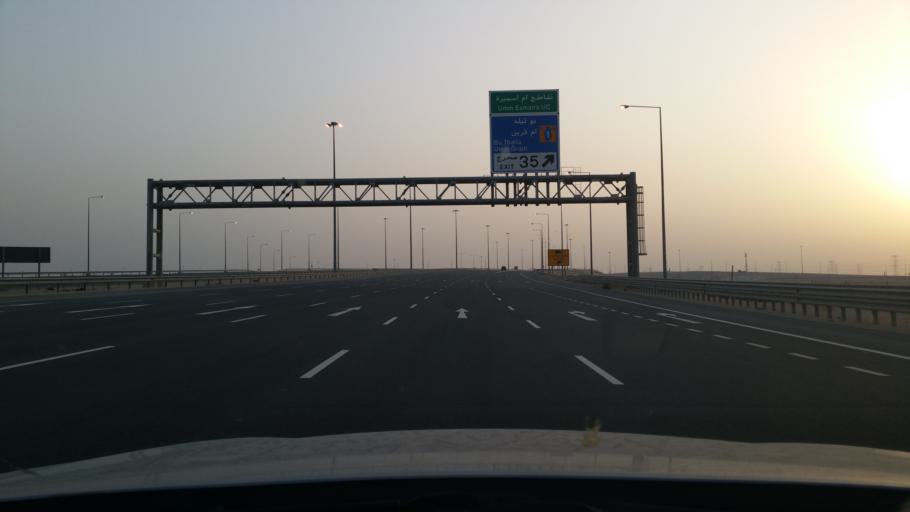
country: QA
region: Baladiyat az Za`ayin
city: Az Za`ayin
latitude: 25.6449
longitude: 51.4029
